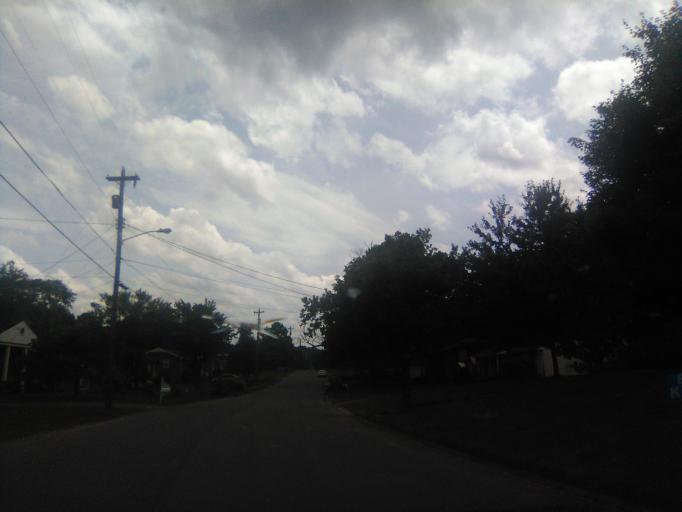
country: US
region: Tennessee
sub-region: Davidson County
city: Belle Meade
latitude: 36.0905
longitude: -86.8843
